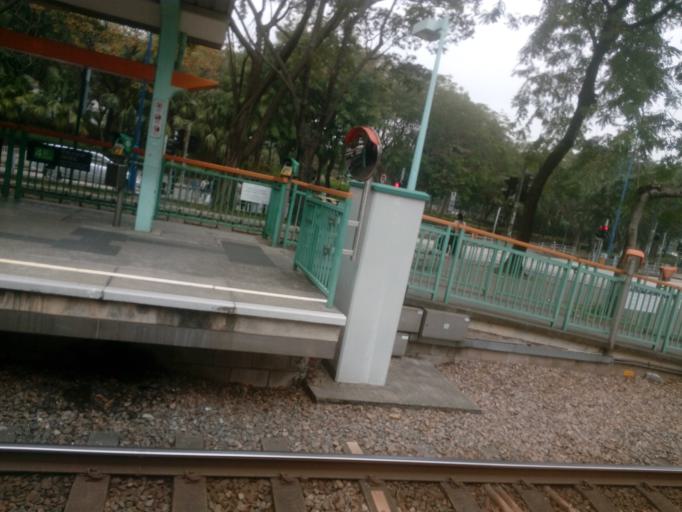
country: HK
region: Yuen Long
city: Yuen Long Kau Hui
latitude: 22.4557
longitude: 113.9995
